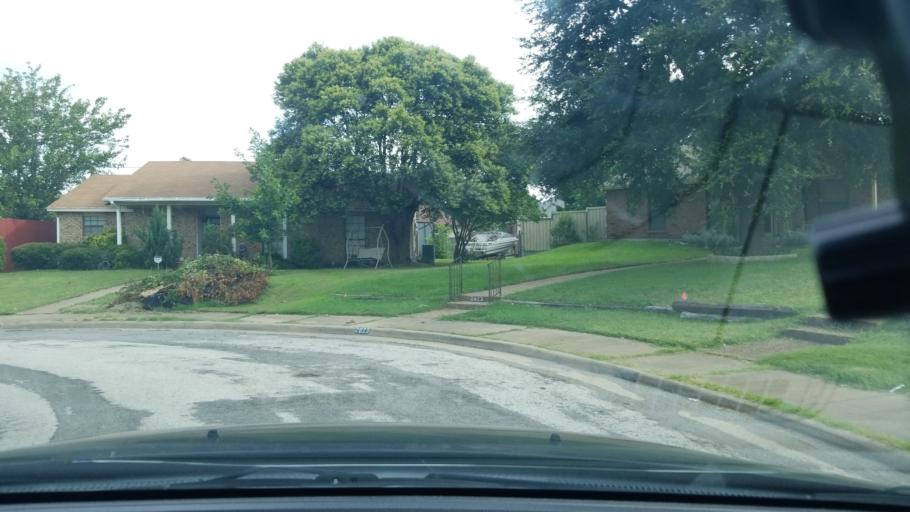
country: US
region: Texas
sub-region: Dallas County
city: Mesquite
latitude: 32.8171
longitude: -96.6661
